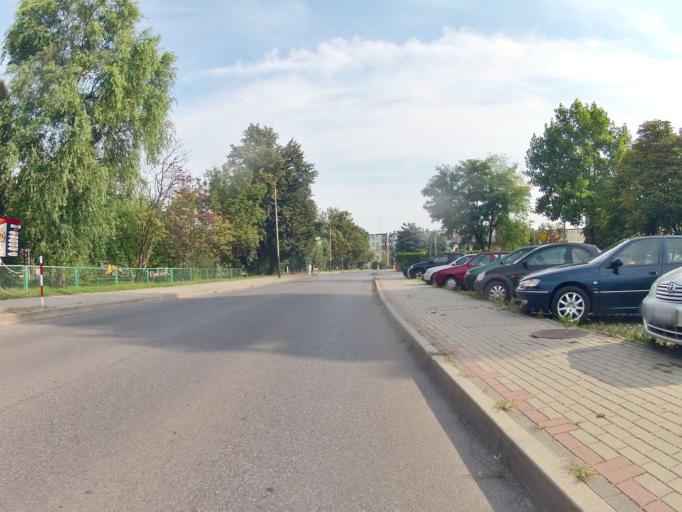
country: PL
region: Subcarpathian Voivodeship
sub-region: Powiat jasielski
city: Jaslo
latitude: 49.7472
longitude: 21.4611
